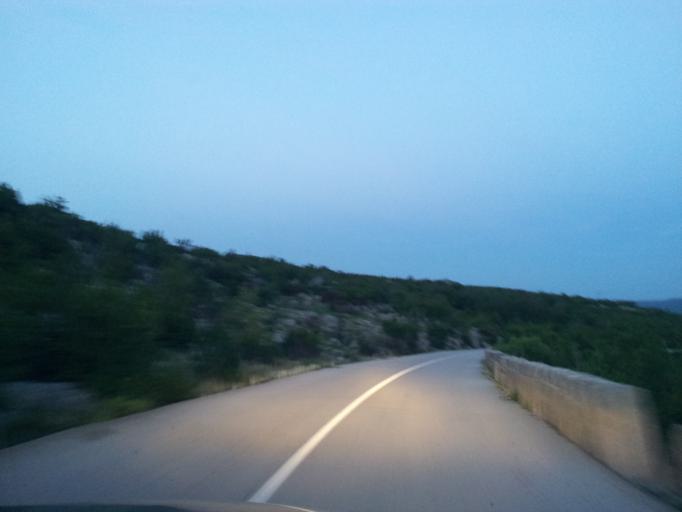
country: HR
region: Zadarska
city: Obrovac
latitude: 44.2288
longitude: 15.6720
